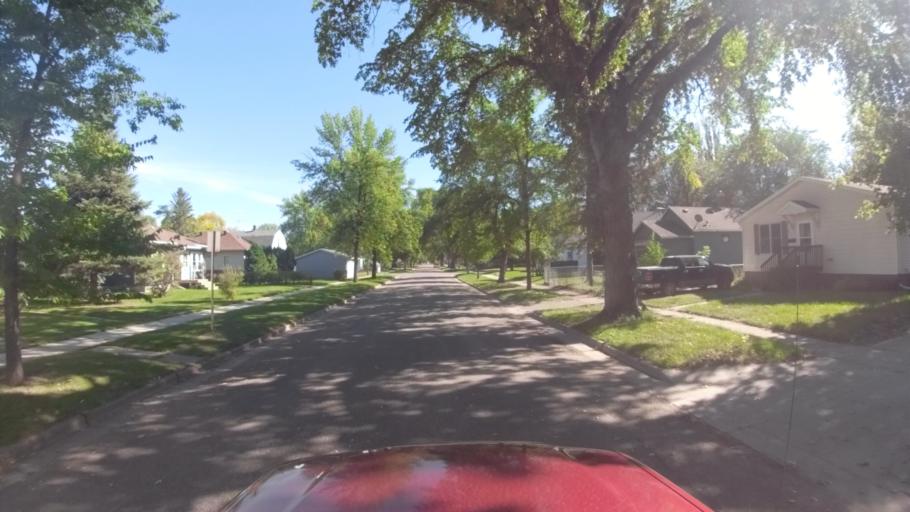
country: US
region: North Dakota
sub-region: Grand Forks County
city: Grand Forks
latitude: 47.9290
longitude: -97.0443
